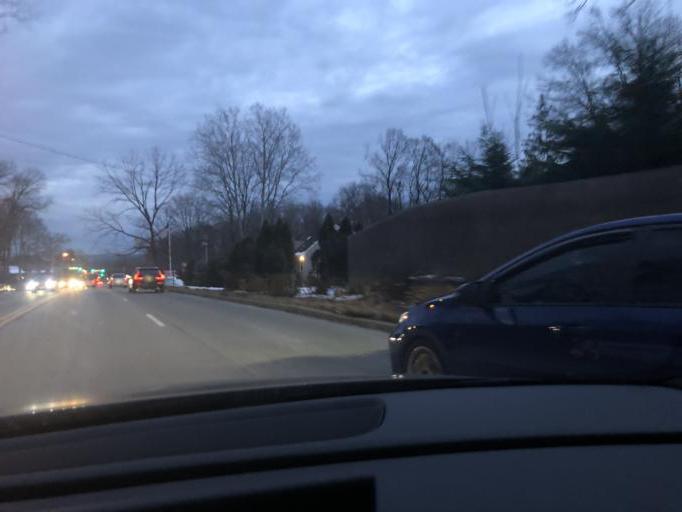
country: US
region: New Jersey
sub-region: Morris County
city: Morristown
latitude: 40.7945
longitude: -74.4457
